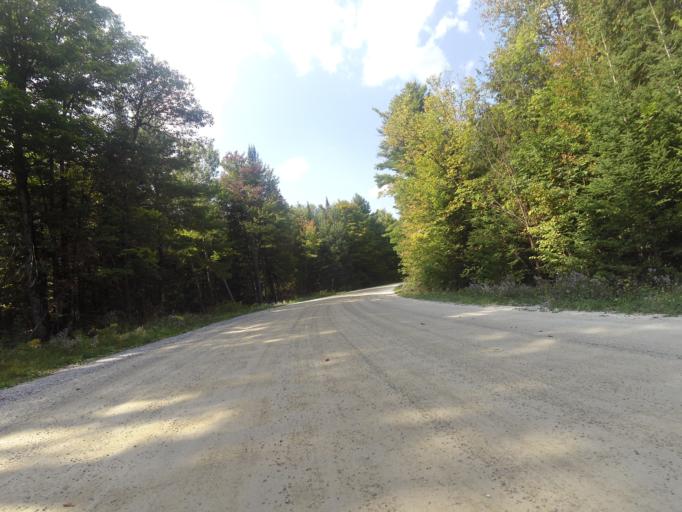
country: CA
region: Ontario
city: Renfrew
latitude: 45.1489
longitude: -76.6777
